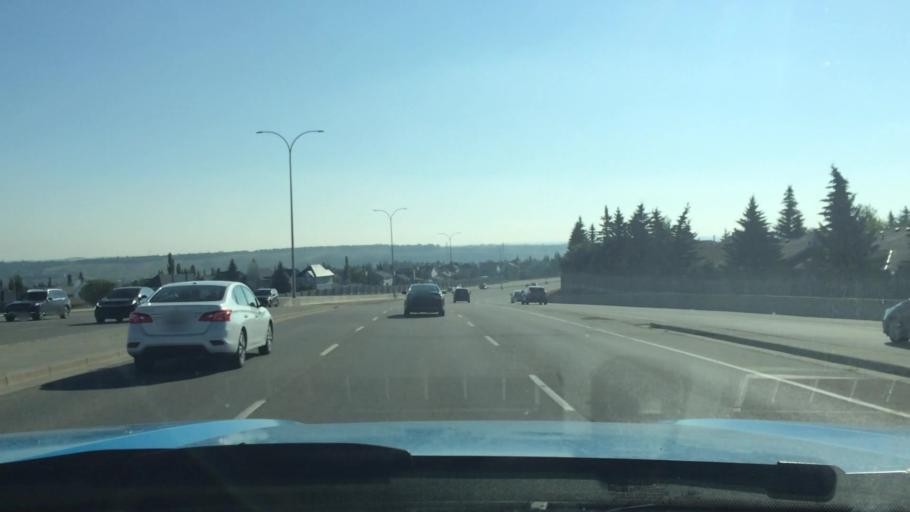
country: CA
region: Alberta
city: Calgary
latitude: 51.1433
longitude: -114.1210
